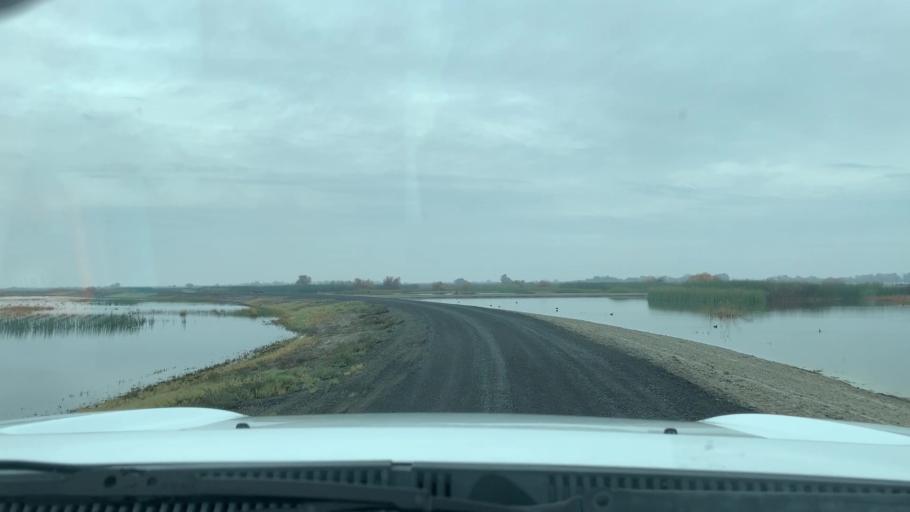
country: US
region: California
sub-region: Kern County
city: Lost Hills
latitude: 35.7421
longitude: -119.6059
